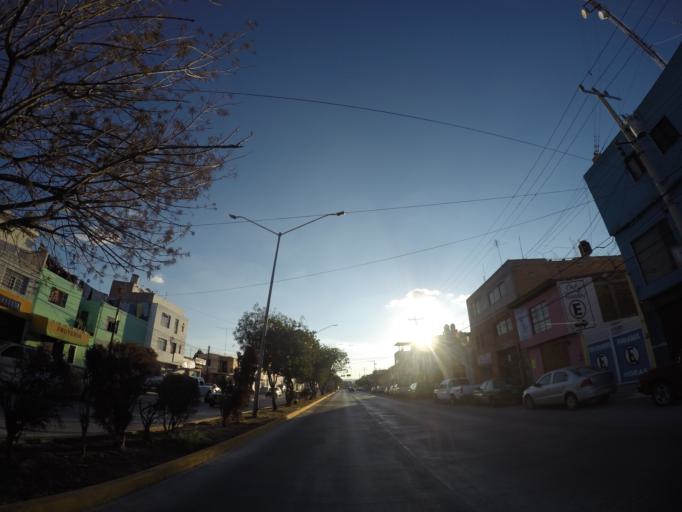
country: MX
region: San Luis Potosi
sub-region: San Luis Potosi
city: San Luis Potosi
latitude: 22.1334
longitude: -100.9716
